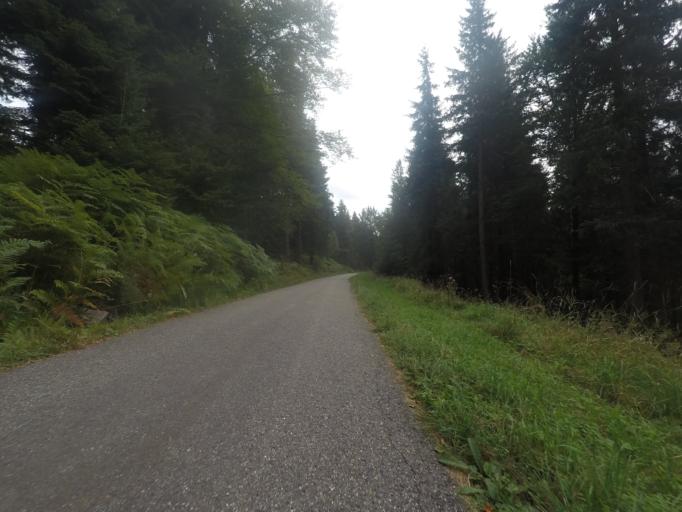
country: DE
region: Baden-Wuerttemberg
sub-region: Karlsruhe Region
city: Dobel
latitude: 48.7788
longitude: 8.4729
